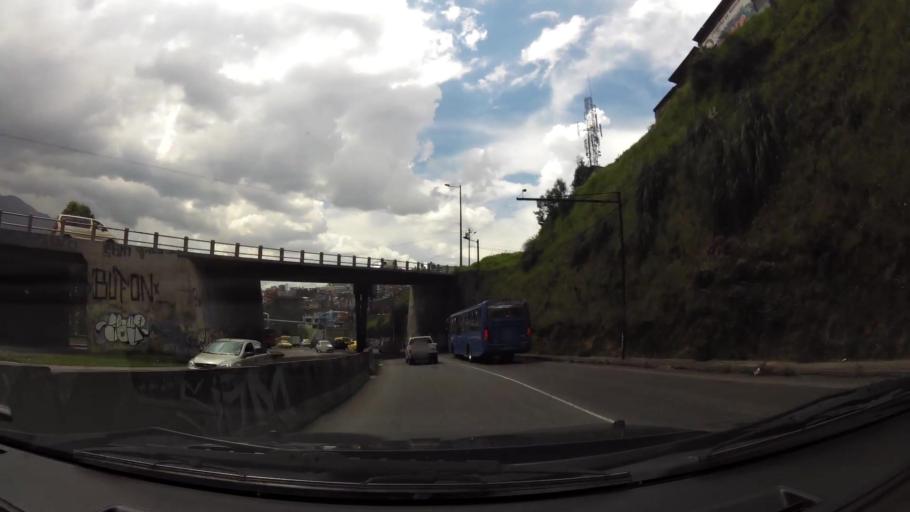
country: EC
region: Pichincha
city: Quito
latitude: -0.2341
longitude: -78.5088
